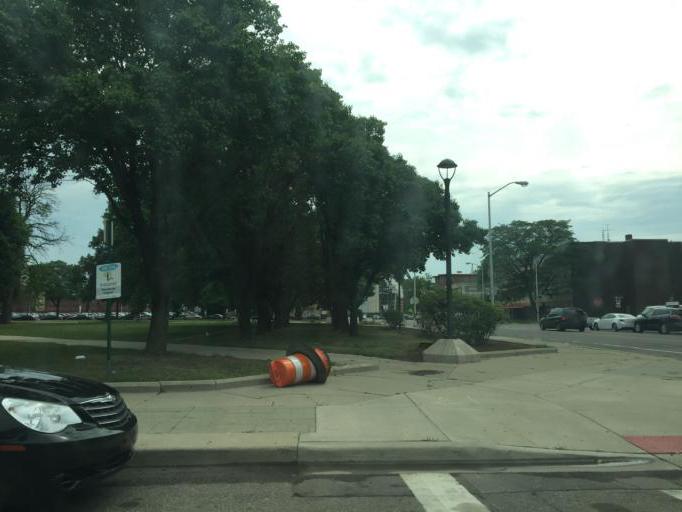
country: US
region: Michigan
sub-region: Wayne County
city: Detroit
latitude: 42.3396
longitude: -83.0609
